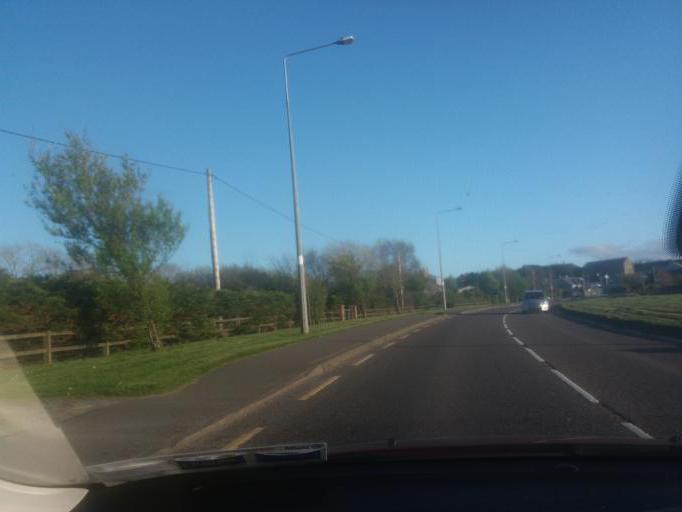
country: IE
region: Munster
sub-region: Ciarrai
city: Killorglin
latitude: 52.1480
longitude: -9.7163
